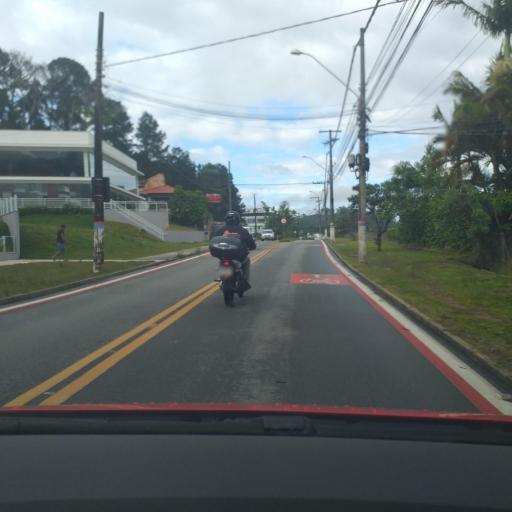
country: BR
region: Santa Catarina
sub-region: Florianopolis
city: Corrego Grande
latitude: -27.5953
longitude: -48.4974
